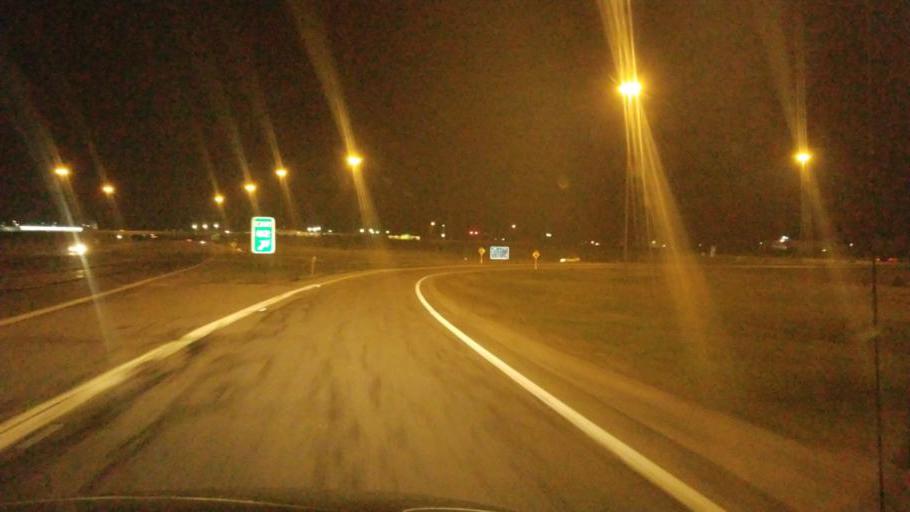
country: US
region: Ohio
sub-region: Fayette County
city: Washington Court House
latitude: 39.5270
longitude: -83.4643
